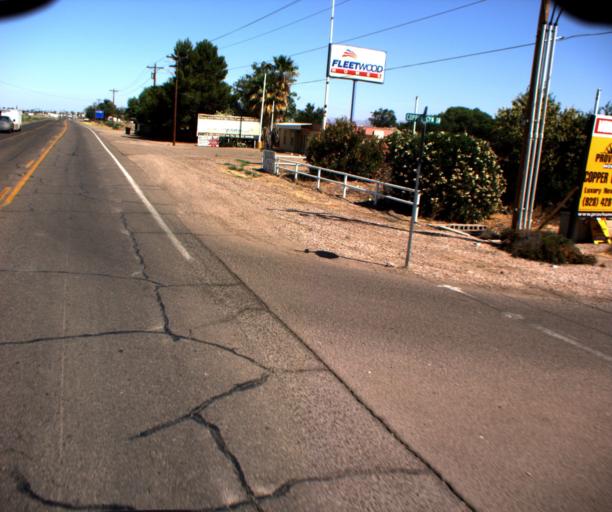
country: US
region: Arizona
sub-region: Graham County
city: Safford
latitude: 32.8241
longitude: -109.6900
